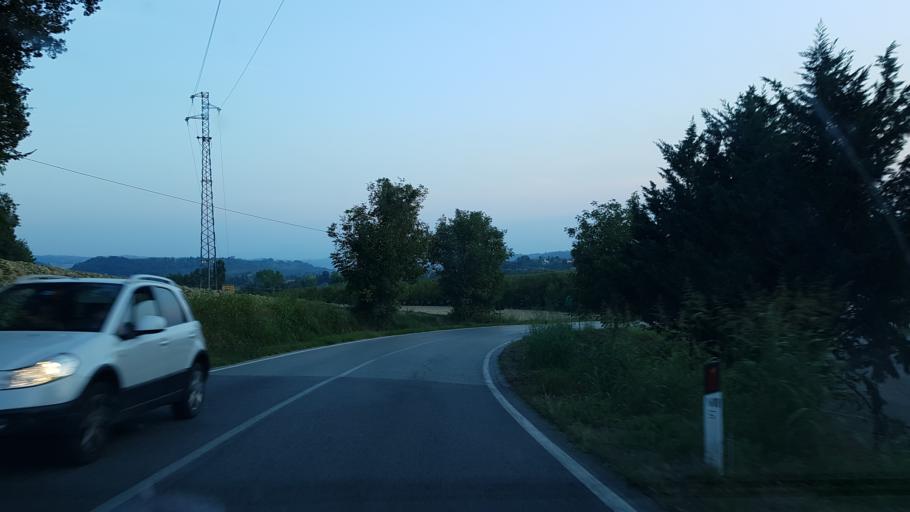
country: IT
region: Piedmont
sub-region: Provincia di Cuneo
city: Novello
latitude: 44.5864
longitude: 7.9059
